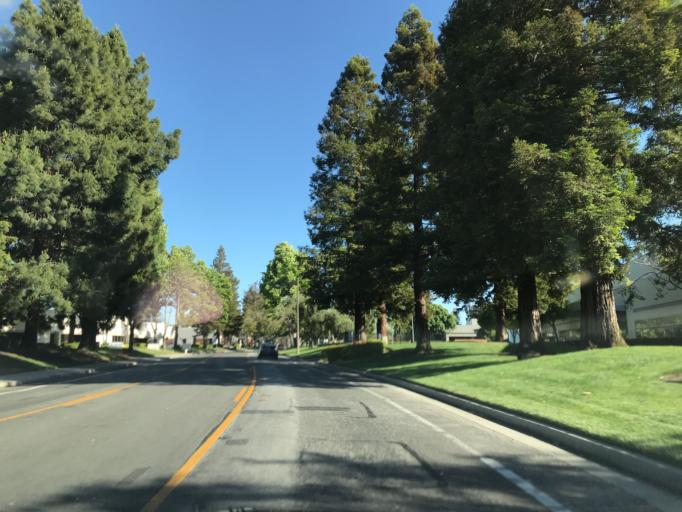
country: US
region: California
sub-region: Santa Clara County
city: Santa Clara
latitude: 37.3834
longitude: -121.9884
